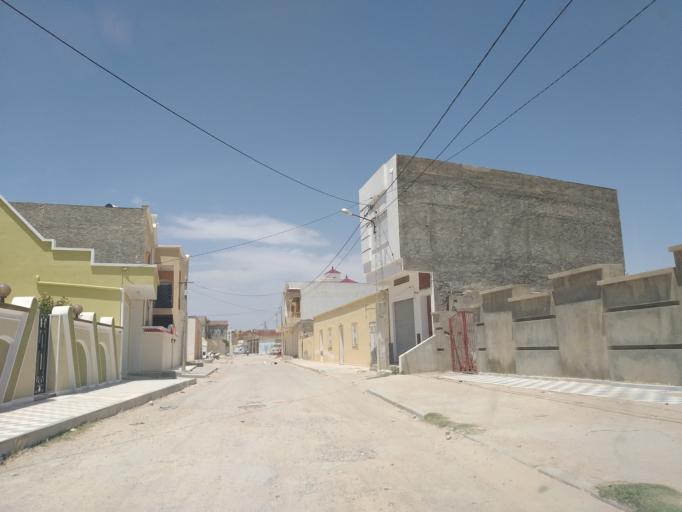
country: TN
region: Al Mahdiyah
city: El Jem
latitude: 35.2952
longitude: 10.6959
